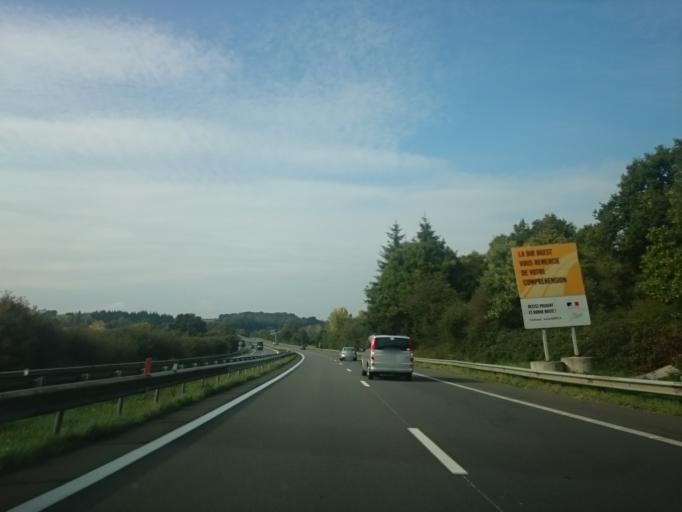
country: FR
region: Brittany
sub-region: Departement d'Ille-et-Vilaine
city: Quedillac
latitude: 48.2651
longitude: -2.1473
